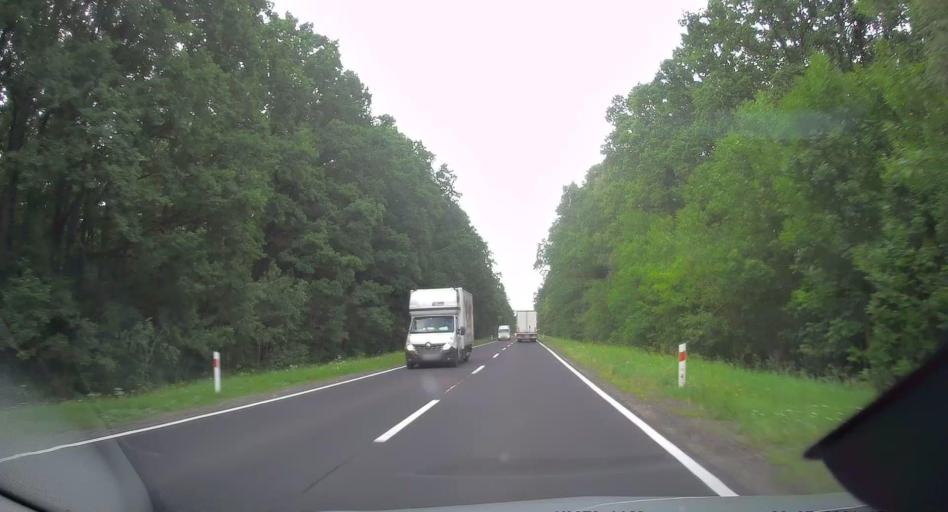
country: PL
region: Silesian Voivodeship
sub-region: Powiat czestochowski
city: Klomnice
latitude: 50.9506
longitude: 19.3982
